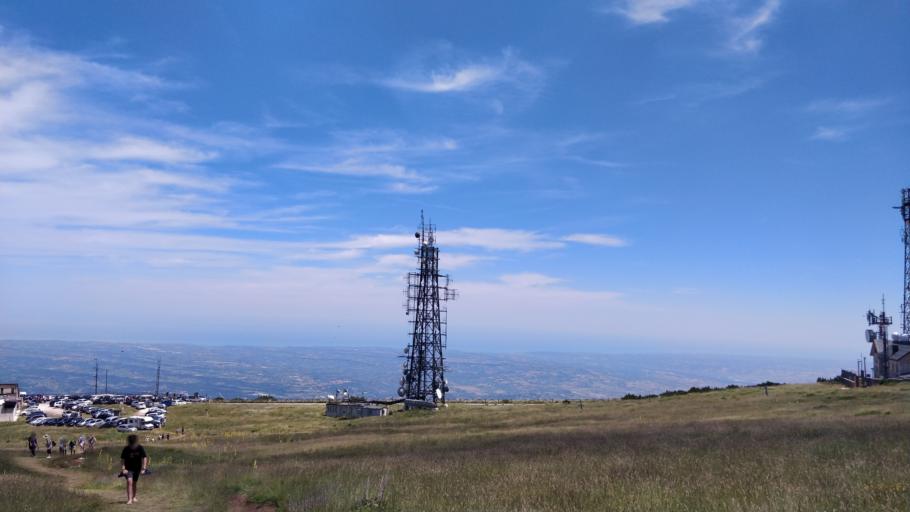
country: IT
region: Abruzzo
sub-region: Provincia di Chieti
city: Pretoro
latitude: 42.1591
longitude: 14.1307
